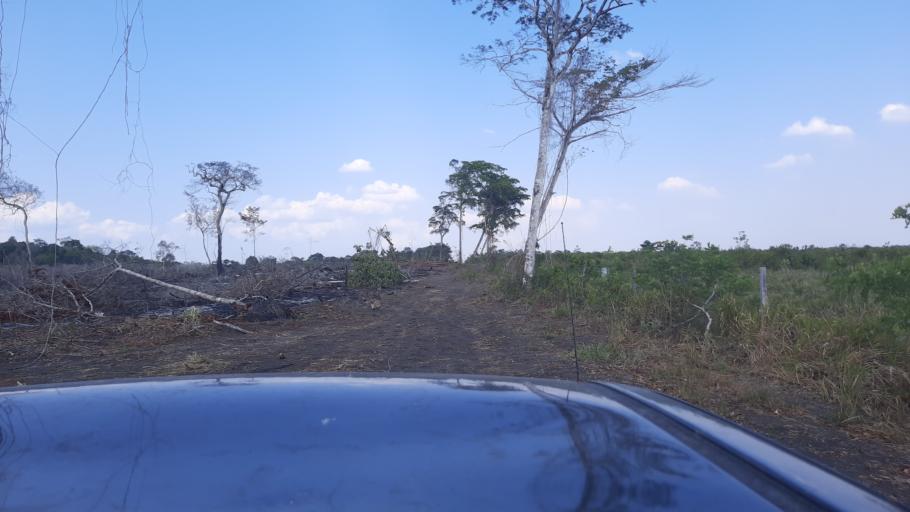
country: BZ
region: Cayo
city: Valley of Peace
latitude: 17.4042
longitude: -89.0368
